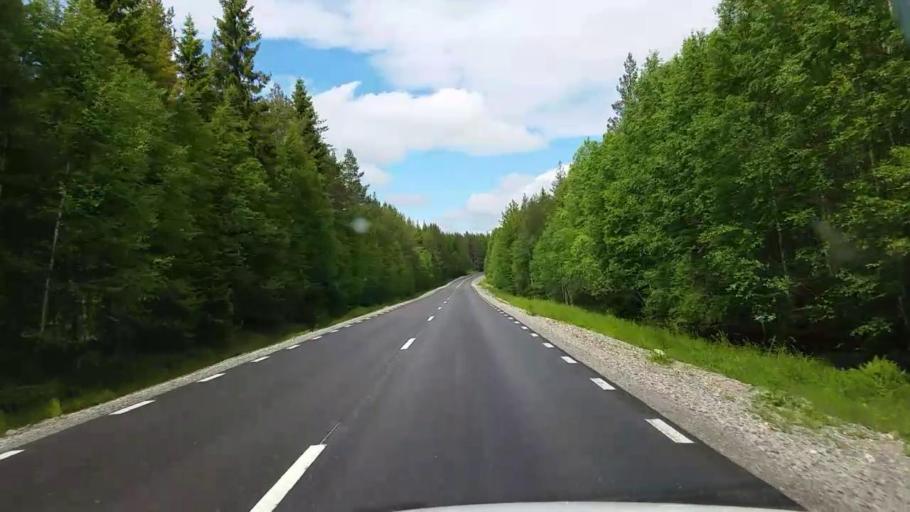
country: SE
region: Gaevleborg
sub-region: Sandvikens Kommun
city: Jarbo
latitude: 60.8943
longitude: 16.3779
